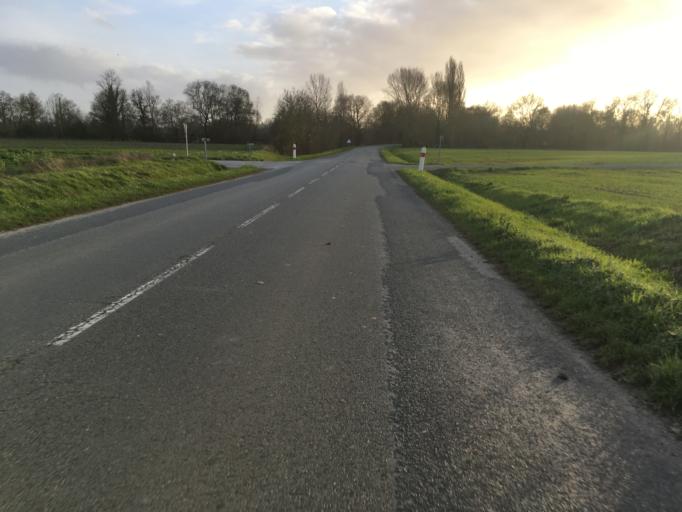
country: FR
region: Poitou-Charentes
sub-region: Departement de la Charente-Maritime
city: Courcon
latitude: 46.1706
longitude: -0.8491
